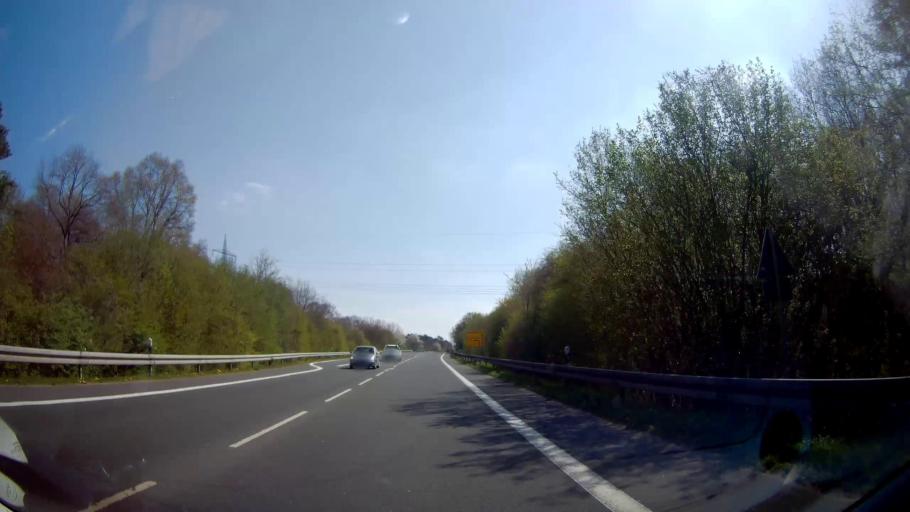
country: DE
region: North Rhine-Westphalia
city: Dorsten
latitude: 51.6861
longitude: 7.0176
